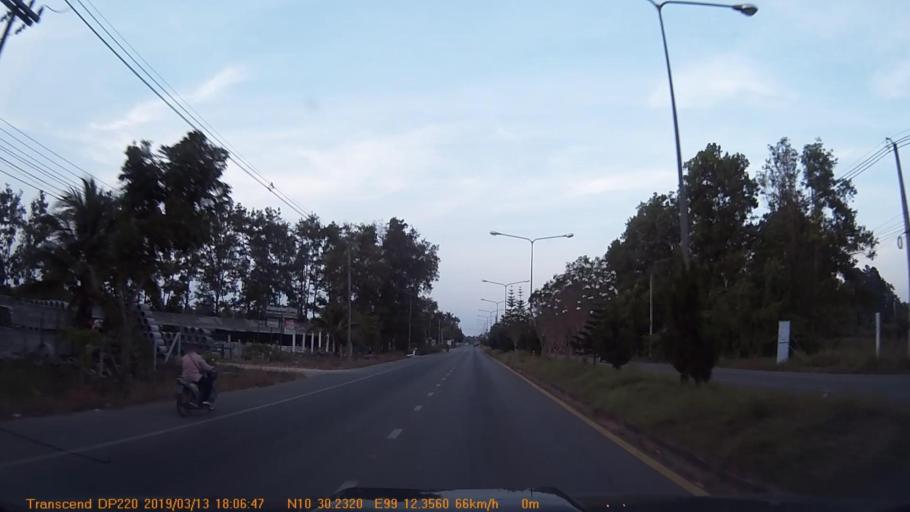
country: TH
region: Chumphon
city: Chumphon
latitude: 10.5041
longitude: 99.2060
